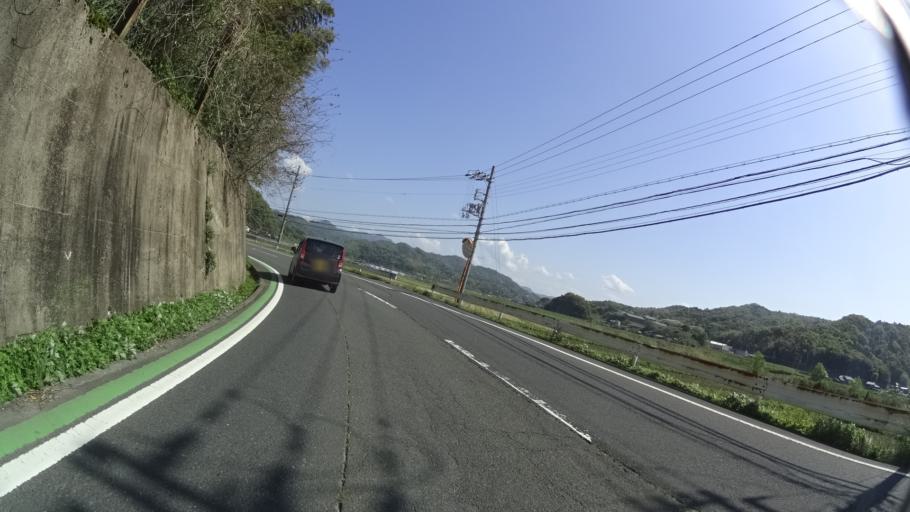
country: JP
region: Kyoto
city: Miyazu
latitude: 35.7265
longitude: 135.1039
